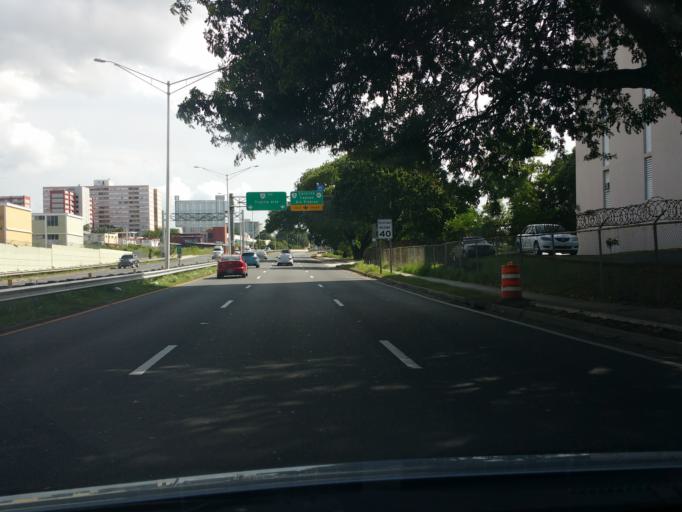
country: PR
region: Trujillo Alto
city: Trujillo Alto
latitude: 18.4043
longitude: -66.0312
